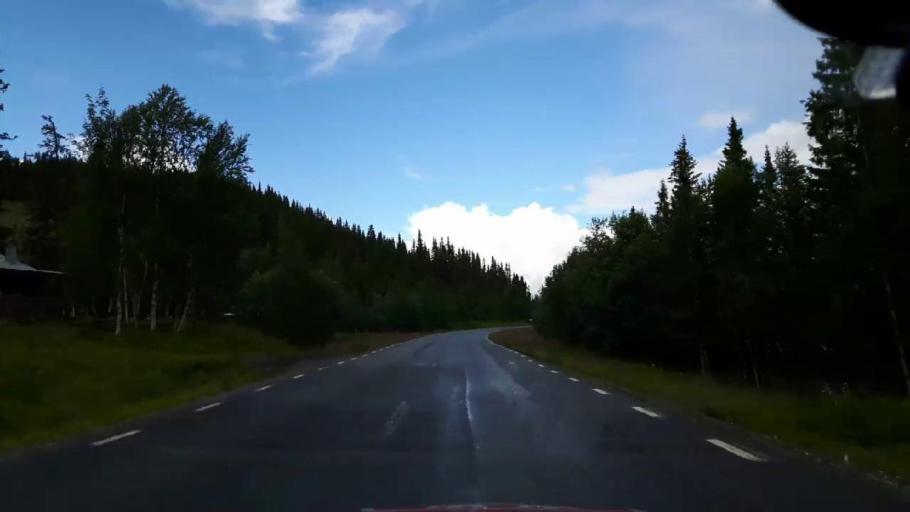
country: SE
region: Vaesterbotten
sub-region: Vilhelmina Kommun
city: Sjoberg
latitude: 64.9980
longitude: 15.2023
